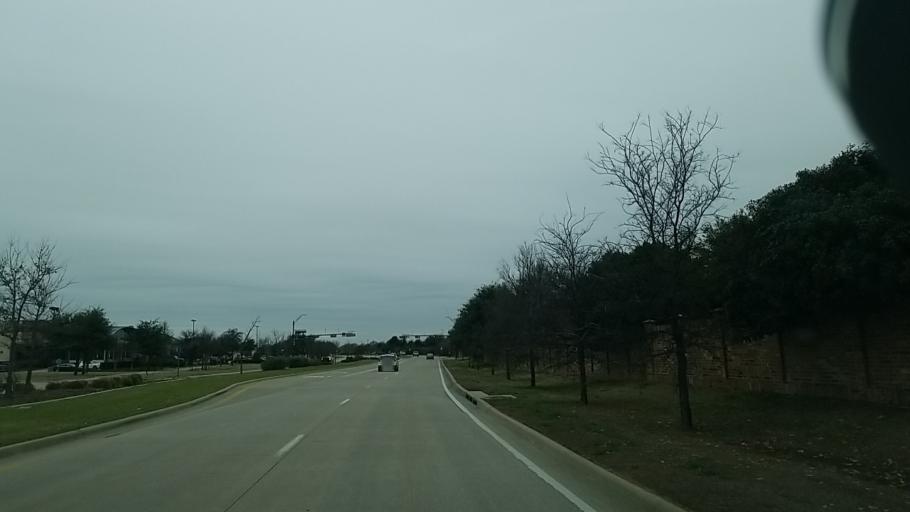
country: US
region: Texas
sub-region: Denton County
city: Copper Canyon
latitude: 33.0783
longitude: -97.0799
